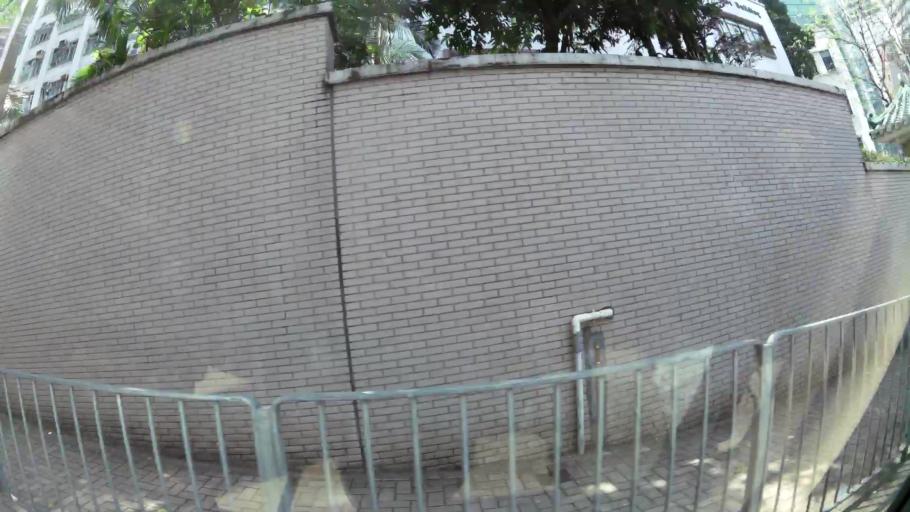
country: HK
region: Wanchai
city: Wan Chai
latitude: 22.2761
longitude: 114.1853
